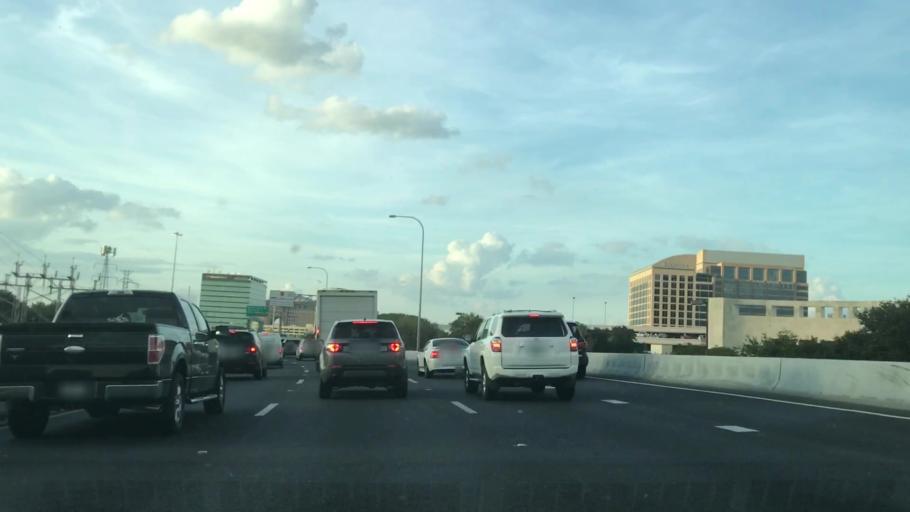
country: US
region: Texas
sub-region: Dallas County
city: Addison
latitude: 32.9301
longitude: -96.8212
